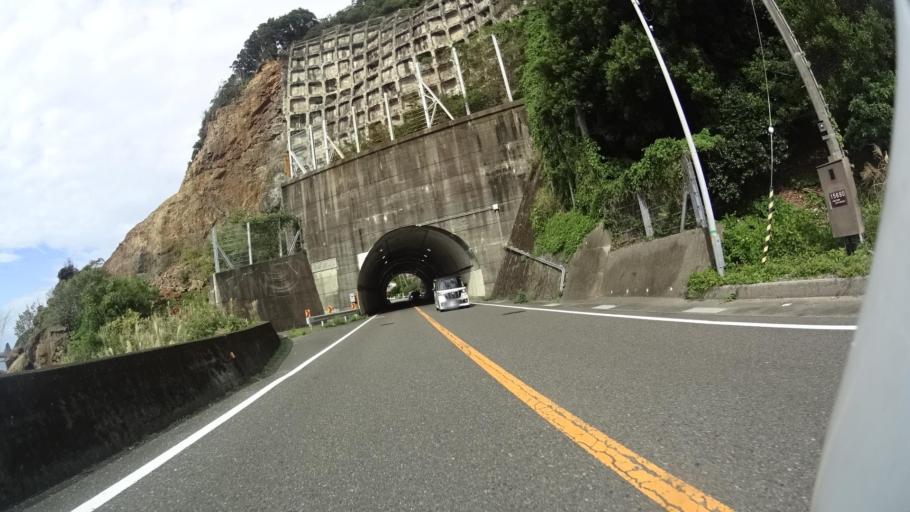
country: JP
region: Wakayama
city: Shingu
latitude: 33.4815
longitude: 135.7508
